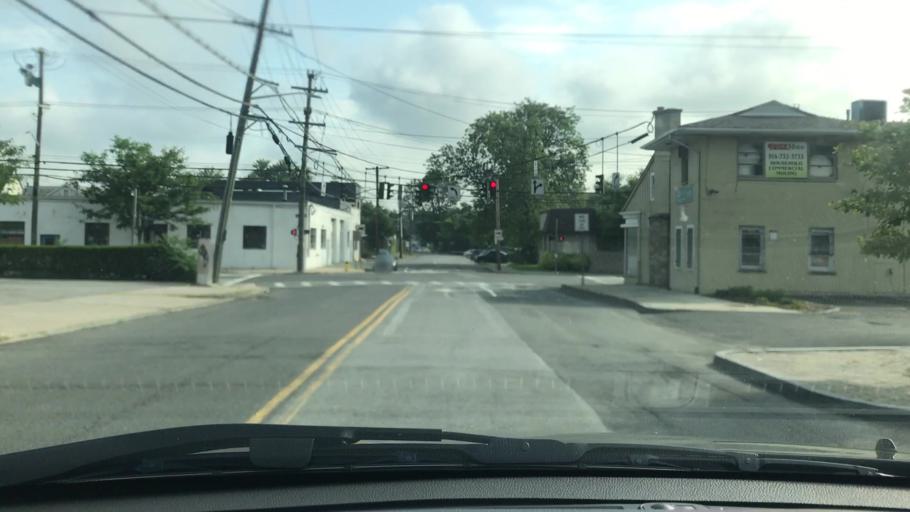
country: US
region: New York
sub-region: Westchester County
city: Mamaroneck
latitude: 40.9502
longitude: -73.7426
